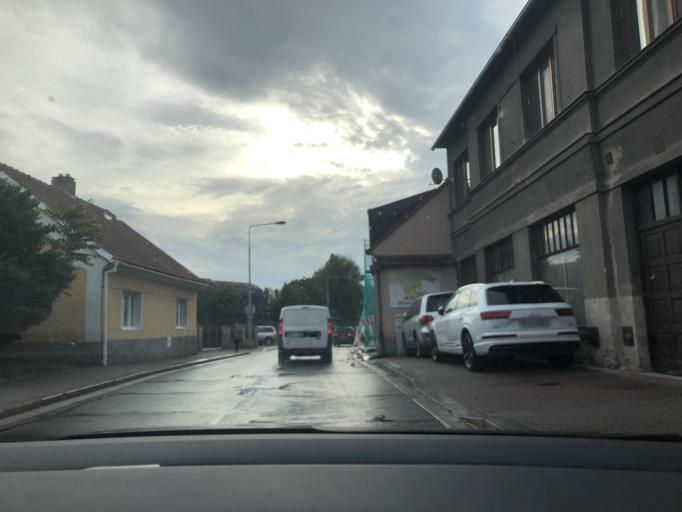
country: CZ
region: Central Bohemia
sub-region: Okres Kolin
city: Kolin
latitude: 50.0316
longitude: 15.2108
